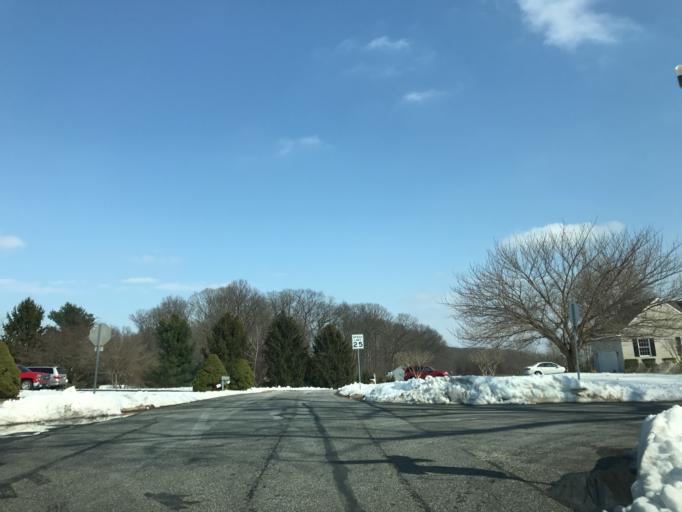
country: US
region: Pennsylvania
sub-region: York County
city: Stewartstown
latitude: 39.6909
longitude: -76.5244
